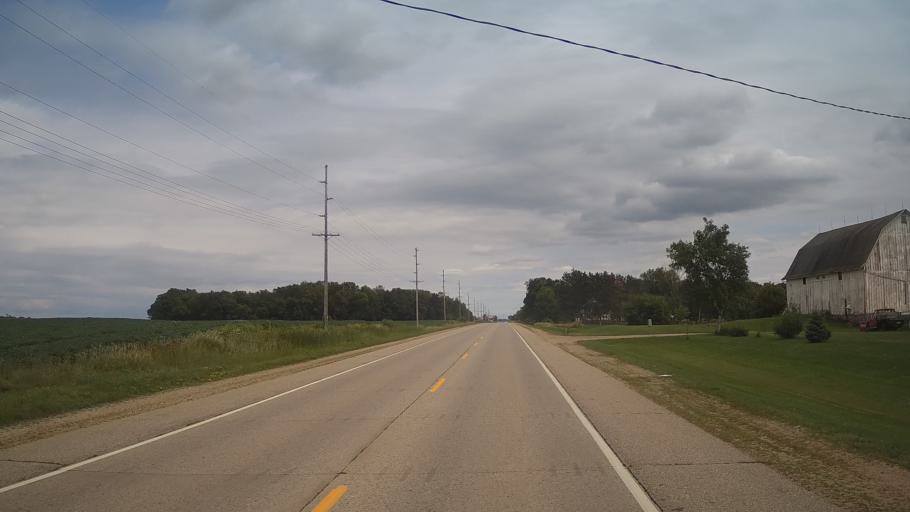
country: US
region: Wisconsin
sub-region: Green Lake County
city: Berlin
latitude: 44.0410
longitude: -89.0036
